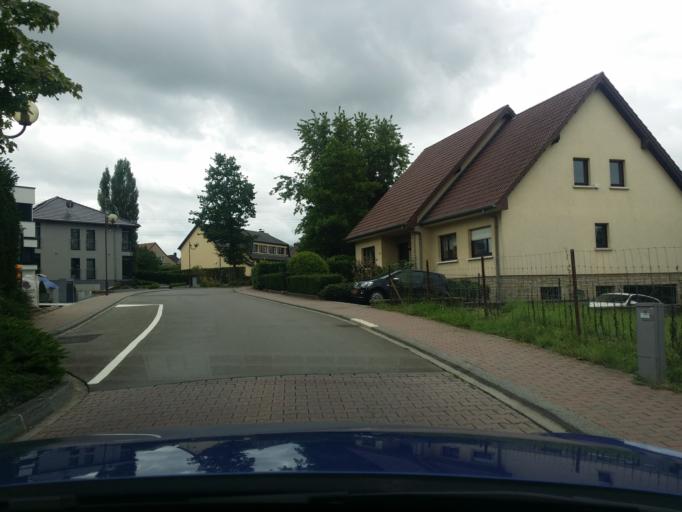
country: LU
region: Luxembourg
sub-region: Canton de Luxembourg
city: Bertrange
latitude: 49.6039
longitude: 6.0520
